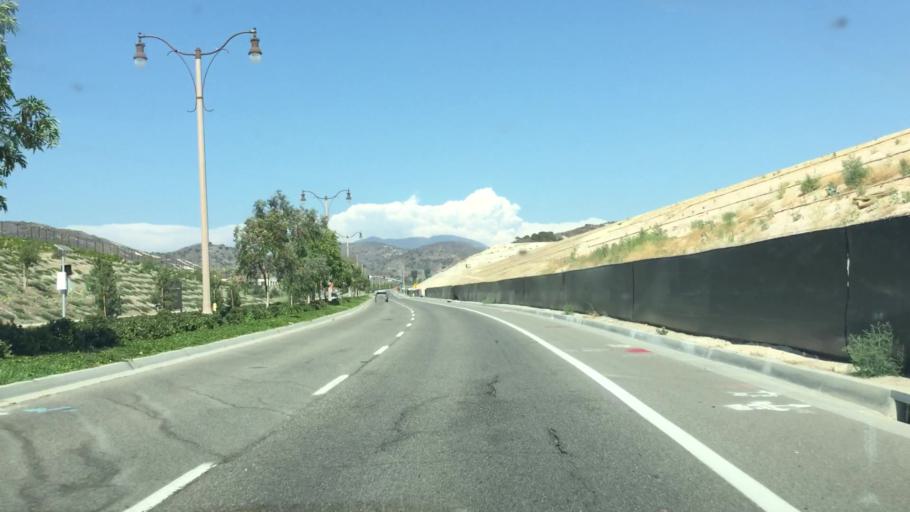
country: US
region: California
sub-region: Orange County
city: Foothill Ranch
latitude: 33.6941
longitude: -117.7050
